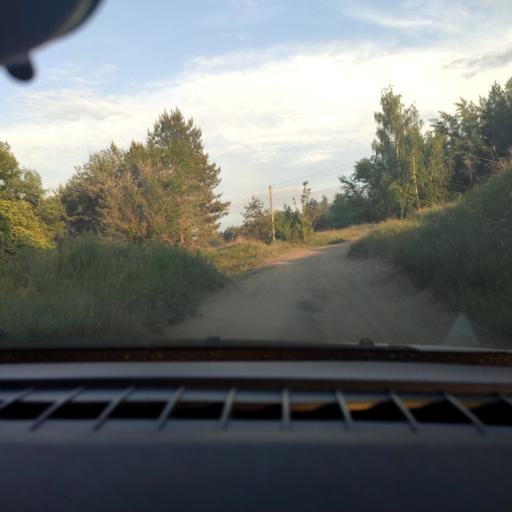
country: RU
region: Voronezj
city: Shilovo
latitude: 51.5357
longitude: 39.1293
